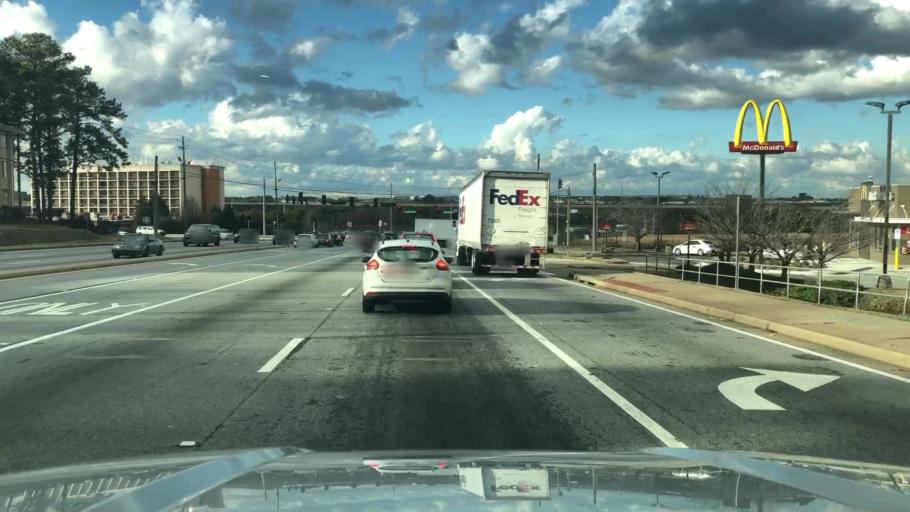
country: US
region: Georgia
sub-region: Fulton County
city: College Park
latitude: 33.6136
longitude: -84.4376
